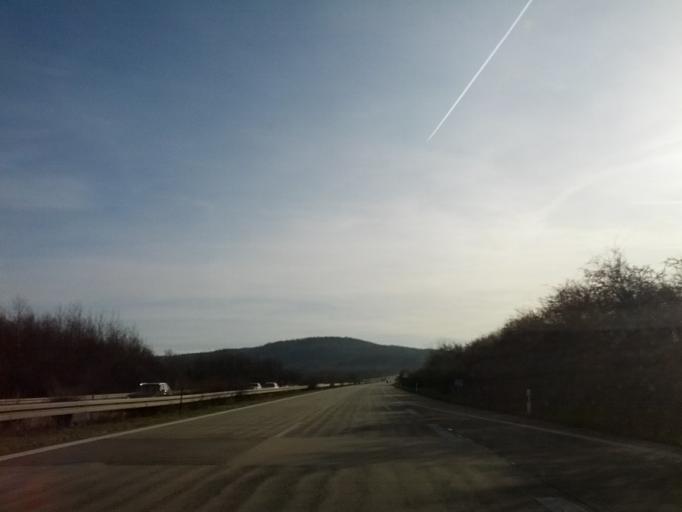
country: DE
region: Bavaria
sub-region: Regierungsbezirk Mittelfranken
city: Gallmersgarten
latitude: 49.4468
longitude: 10.2509
